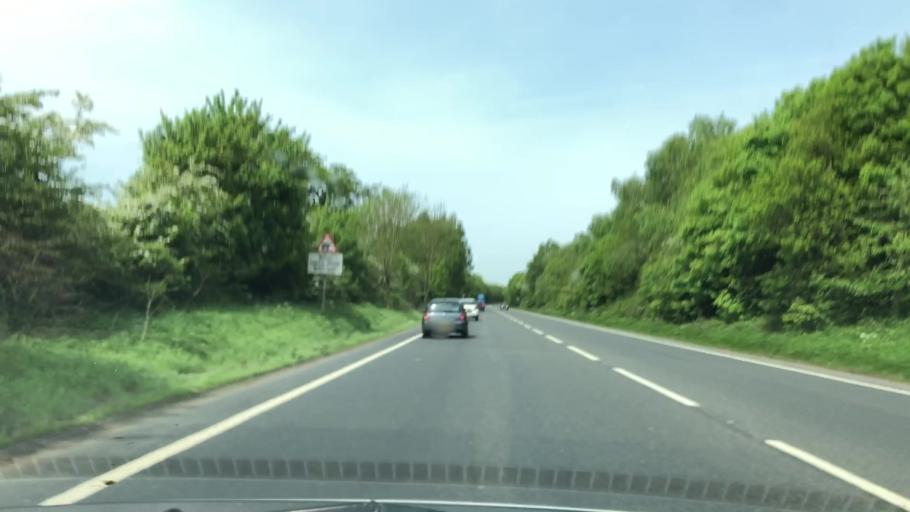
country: GB
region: England
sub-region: Shropshire
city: Gobowen
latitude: 52.8937
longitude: -3.0421
